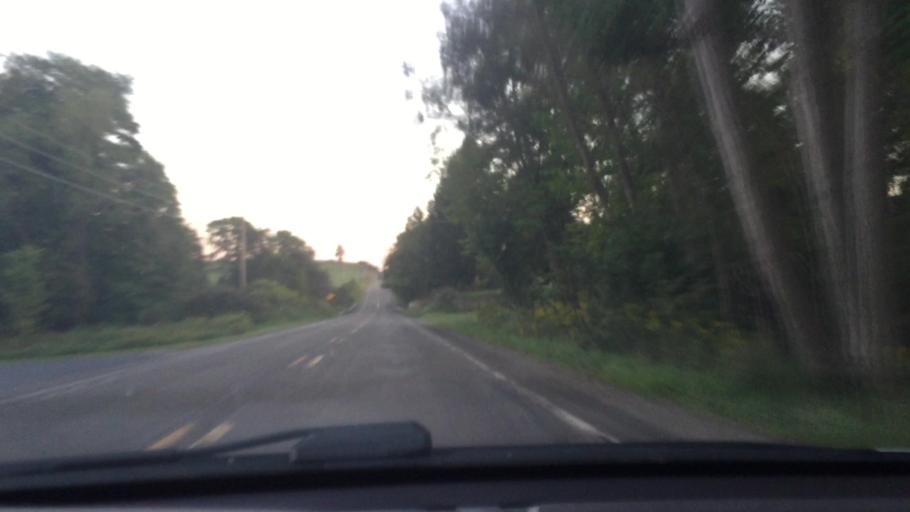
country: US
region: Pennsylvania
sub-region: Butler County
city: Slippery Rock
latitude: 41.0946
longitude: -80.0517
